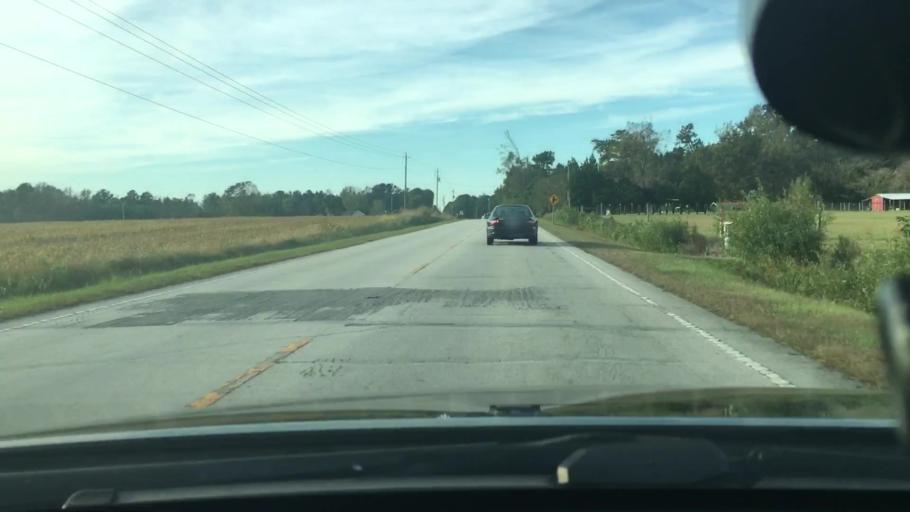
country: US
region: North Carolina
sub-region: Craven County
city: Vanceboro
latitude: 35.3384
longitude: -77.1755
